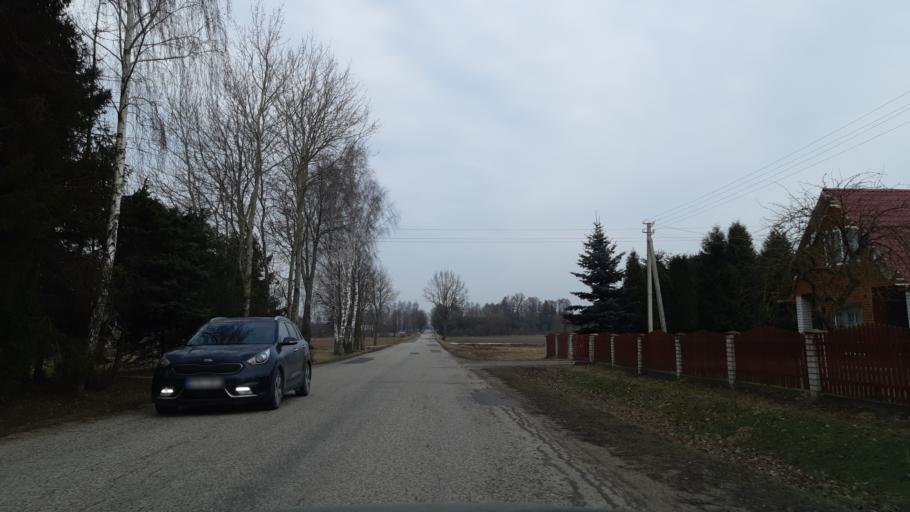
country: LT
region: Marijampoles apskritis
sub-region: Marijampole Municipality
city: Marijampole
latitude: 54.7103
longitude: 23.3155
